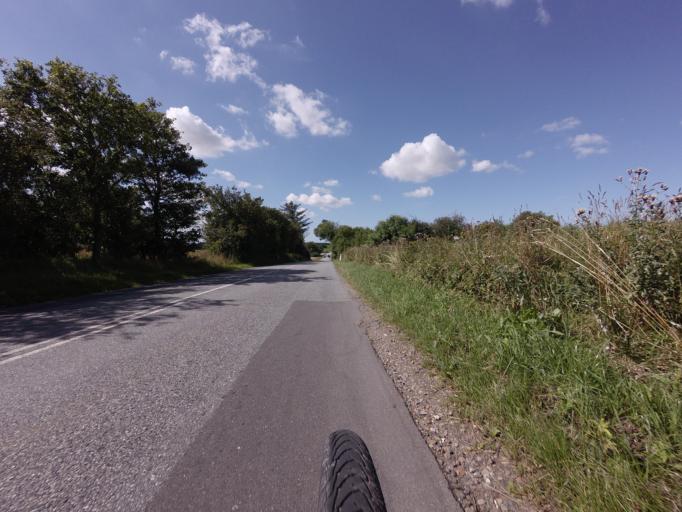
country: DK
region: North Denmark
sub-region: Hjorring Kommune
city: Hjorring
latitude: 57.4813
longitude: 9.9181
